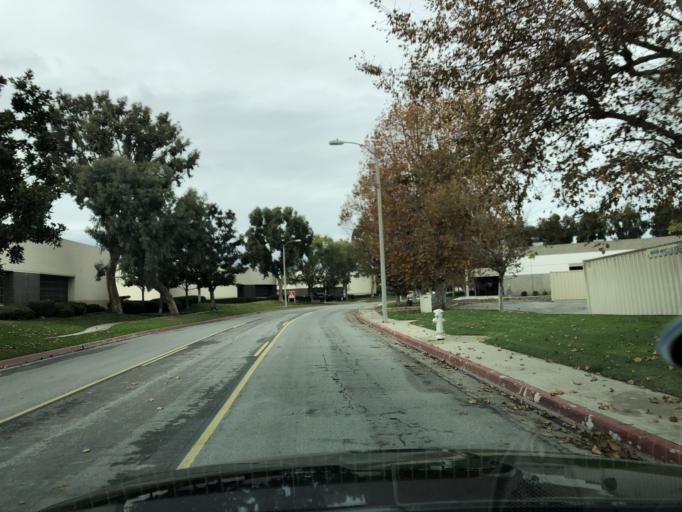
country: US
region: California
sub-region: Orange County
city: Fountain Valley
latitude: 33.6962
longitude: -117.9306
